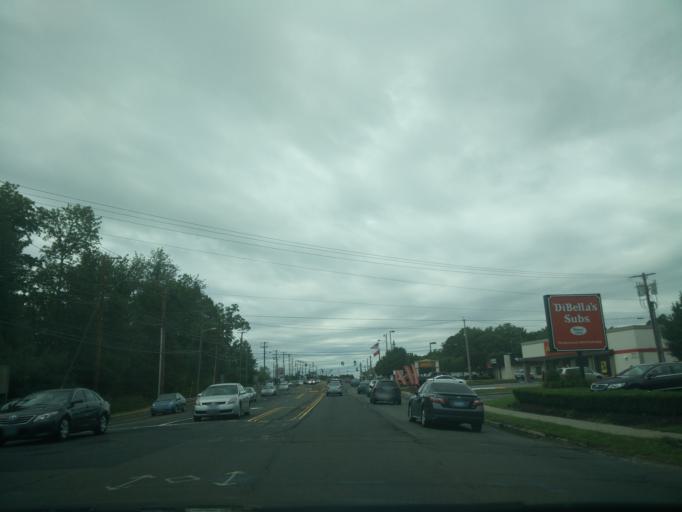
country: US
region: Connecticut
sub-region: New Haven County
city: Milford
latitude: 41.2420
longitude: -73.0320
